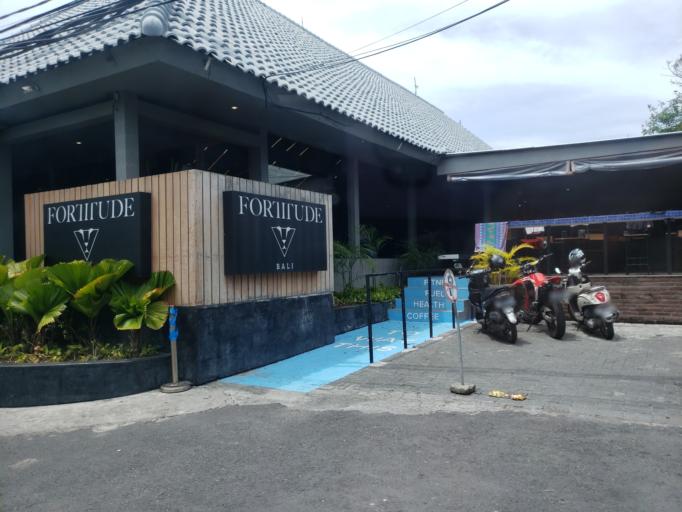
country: ID
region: Bali
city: Kuta
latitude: -8.6805
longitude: 115.1529
